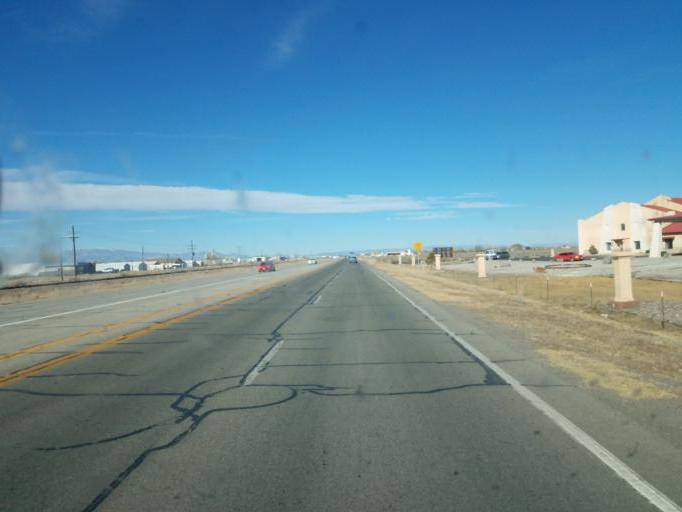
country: US
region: Colorado
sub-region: Alamosa County
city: Alamosa
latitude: 37.4827
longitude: -105.9123
